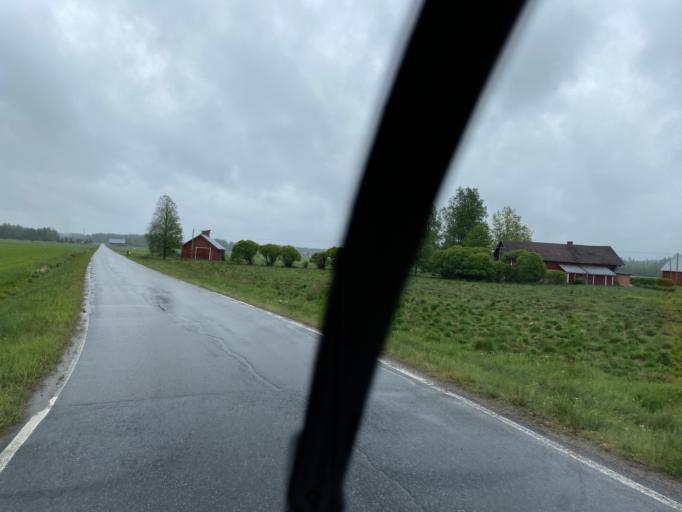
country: FI
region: Haeme
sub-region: Forssa
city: Humppila
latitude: 61.0552
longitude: 23.3264
